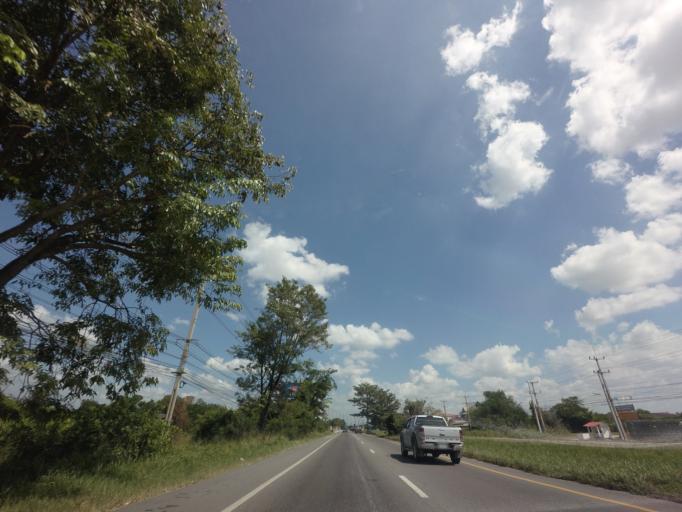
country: TH
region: Chon Buri
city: Ban Bueng
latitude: 13.2993
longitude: 101.1542
